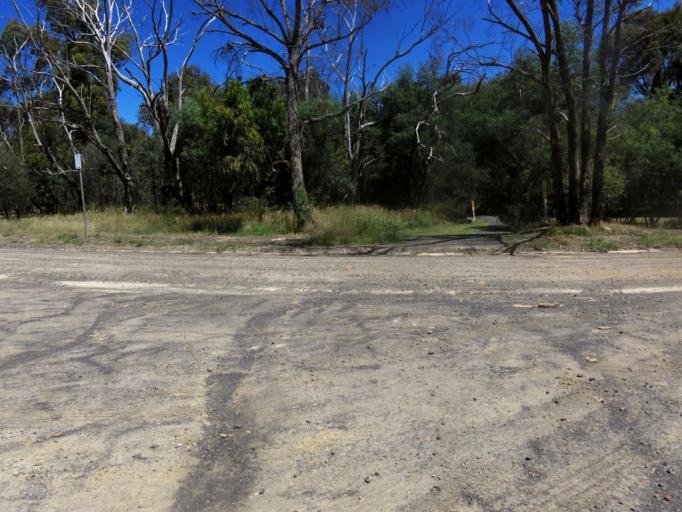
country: AU
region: Victoria
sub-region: Whittlesea
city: Whittlesea
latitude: -37.3609
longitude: 145.0349
